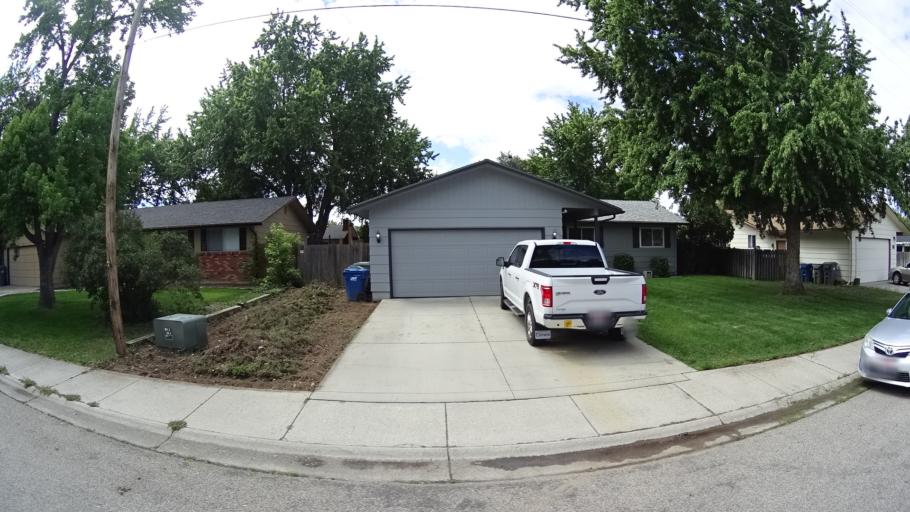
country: US
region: Idaho
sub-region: Ada County
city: Boise
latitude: 43.5715
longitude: -116.1663
